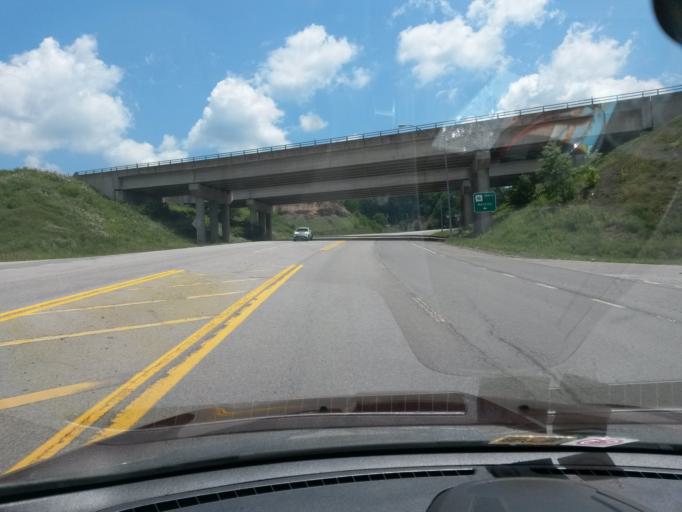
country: US
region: West Virginia
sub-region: Raleigh County
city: Sophia
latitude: 37.7190
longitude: -81.2555
